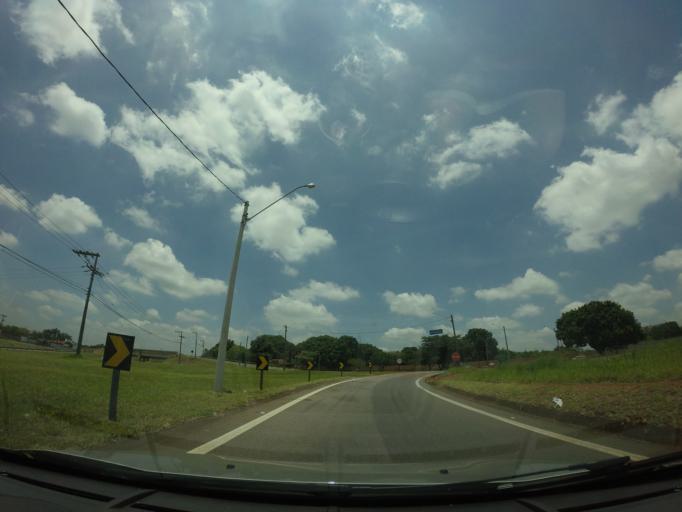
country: BR
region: Sao Paulo
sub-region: Piracicaba
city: Piracicaba
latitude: -22.7628
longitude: -47.5964
